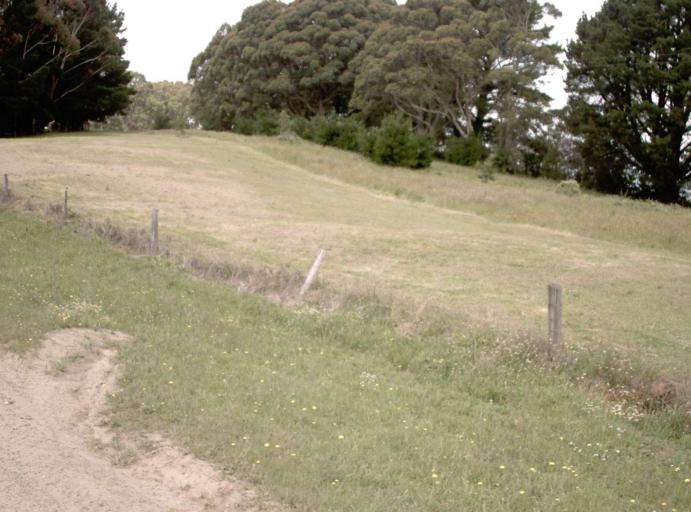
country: AU
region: Victoria
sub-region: Latrobe
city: Traralgon
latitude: -38.3724
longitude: 146.6882
